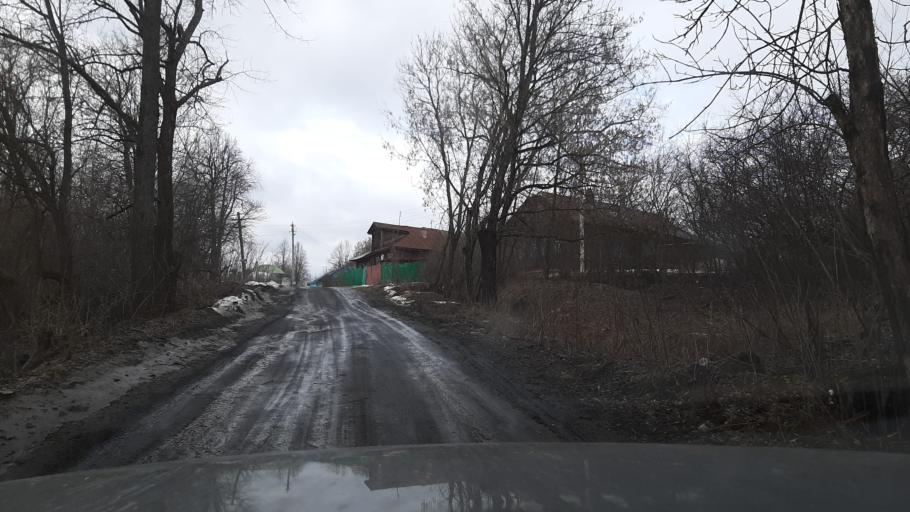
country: RU
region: Ivanovo
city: Teykovo
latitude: 56.8965
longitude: 40.6653
